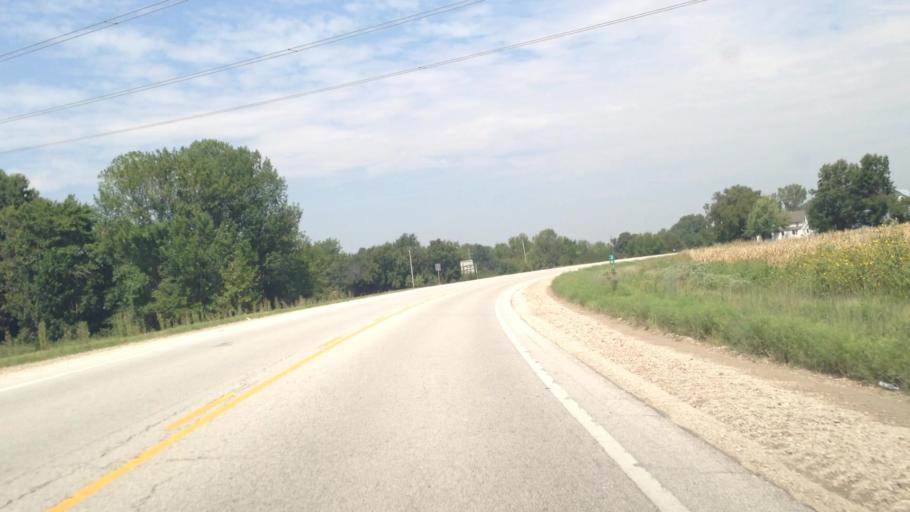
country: US
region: Kansas
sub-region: Labette County
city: Parsons
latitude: 37.3896
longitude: -95.2689
